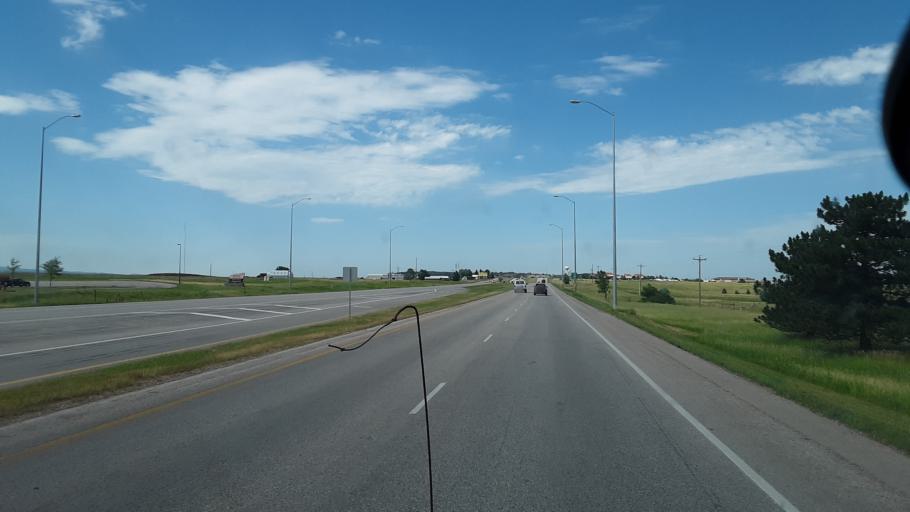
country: US
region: South Dakota
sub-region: Pennington County
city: Colonial Pine Hills
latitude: 44.0047
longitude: -103.2522
